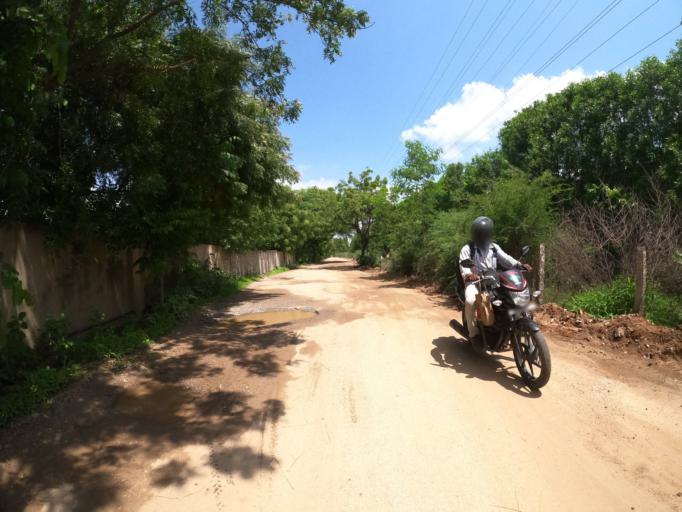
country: IN
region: Telangana
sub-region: Medak
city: Serilingampalle
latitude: 17.3740
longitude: 78.3234
